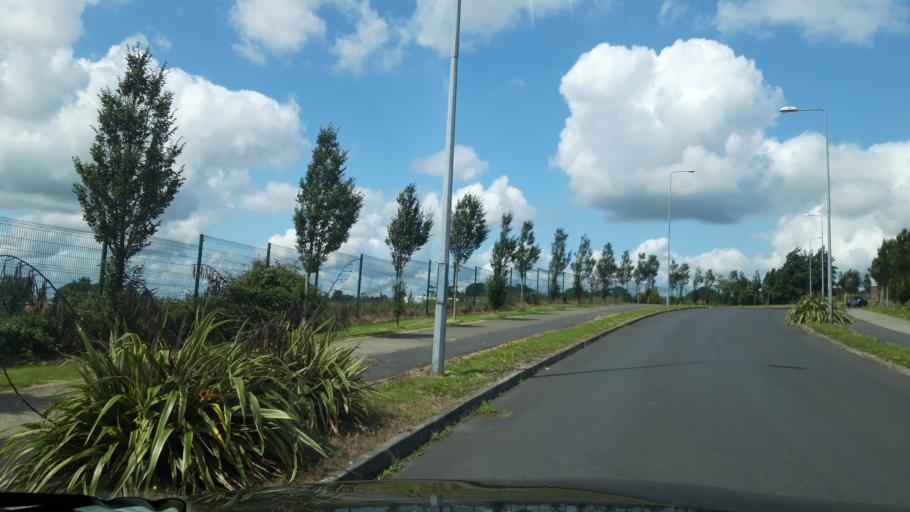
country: IE
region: Munster
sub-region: Waterford
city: Waterford
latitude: 52.2700
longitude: -7.0880
